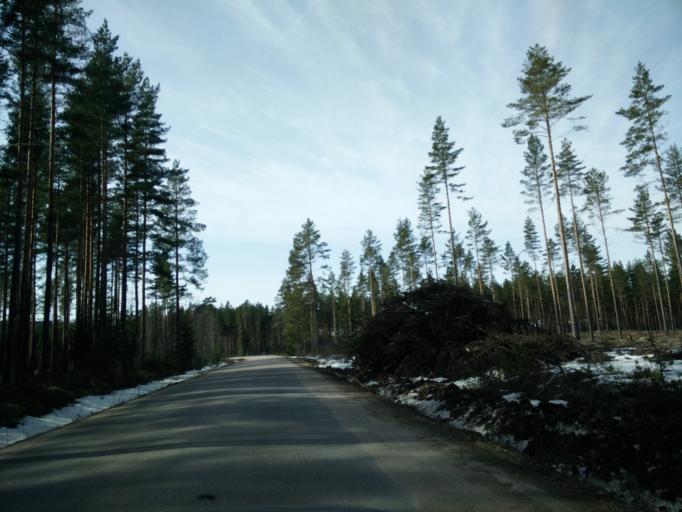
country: SE
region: Vaermland
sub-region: Hagfors Kommun
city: Hagfors
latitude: 60.0441
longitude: 13.5873
